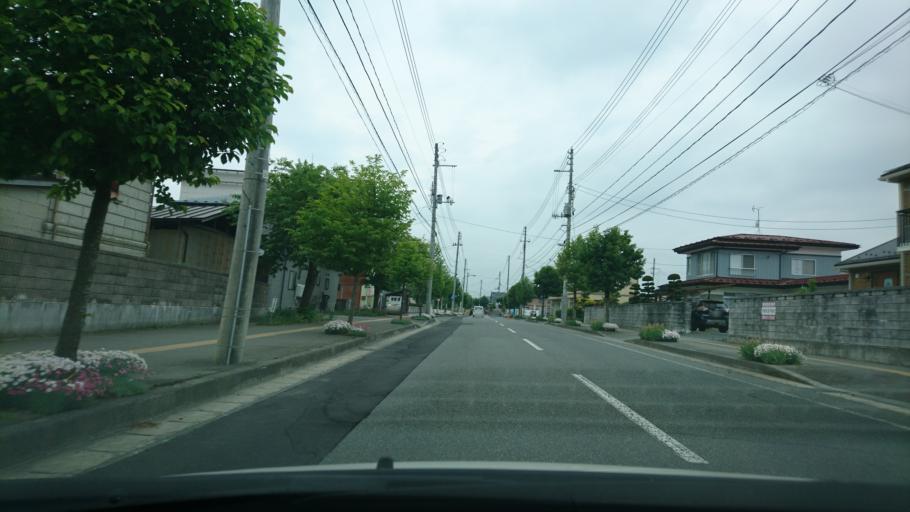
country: JP
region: Iwate
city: Ichinoseki
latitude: 38.9331
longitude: 141.1077
